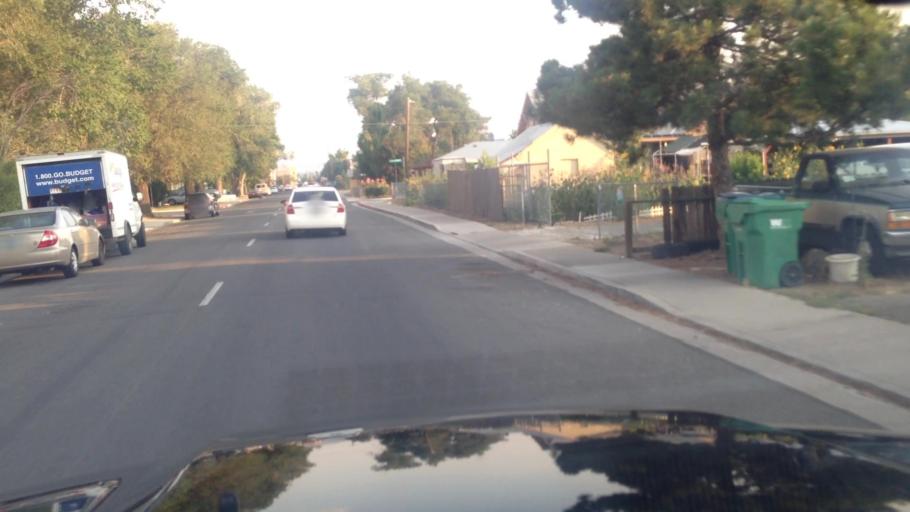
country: US
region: Nevada
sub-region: Washoe County
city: Reno
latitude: 39.5101
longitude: -119.7982
